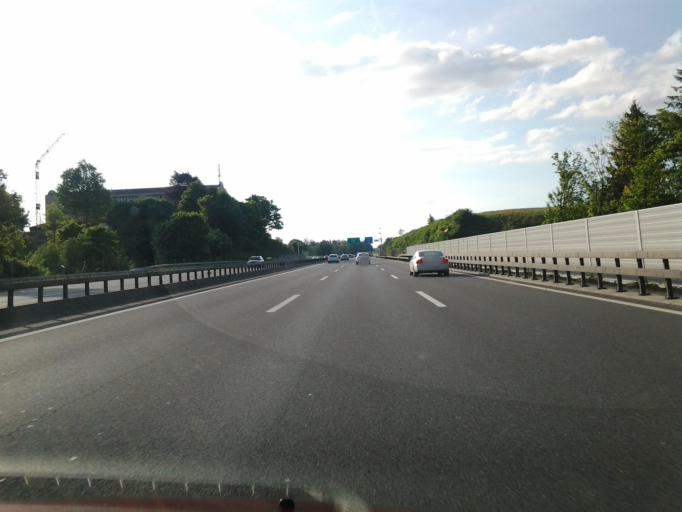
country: CH
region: Lucerne
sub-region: Hochdorf District
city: Emmen
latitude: 47.0854
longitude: 8.2569
